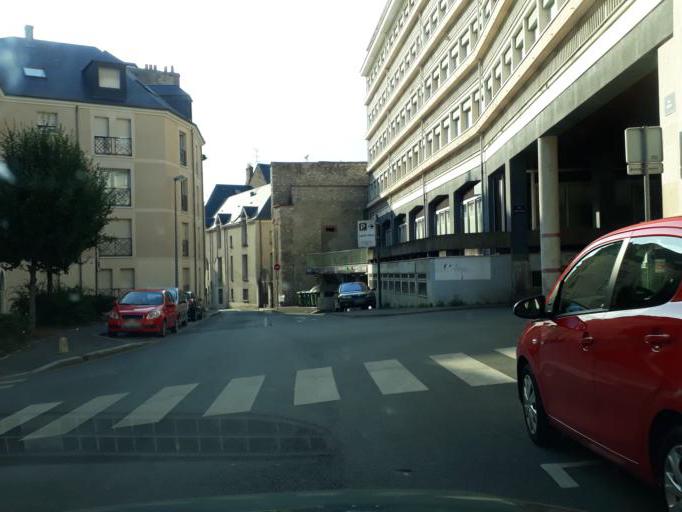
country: FR
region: Centre
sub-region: Departement du Loiret
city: Orleans
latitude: 47.8993
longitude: 1.9018
